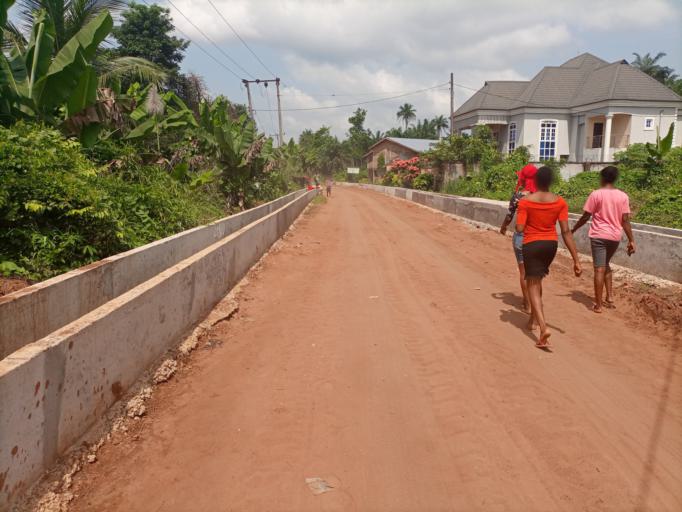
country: NG
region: Imo
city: Ihuo
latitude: 5.5272
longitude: 7.2620
